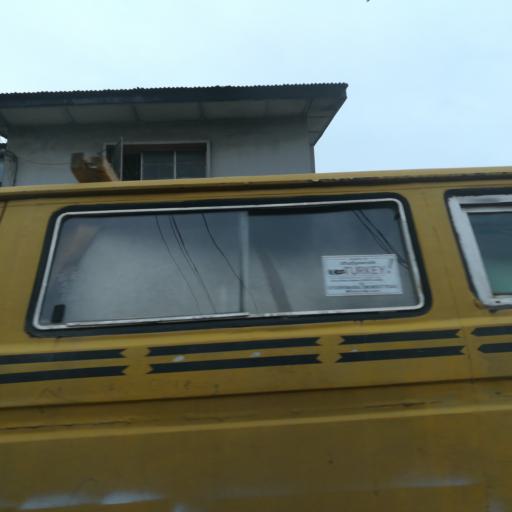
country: NG
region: Lagos
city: Makoko
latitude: 6.4999
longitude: 3.3790
